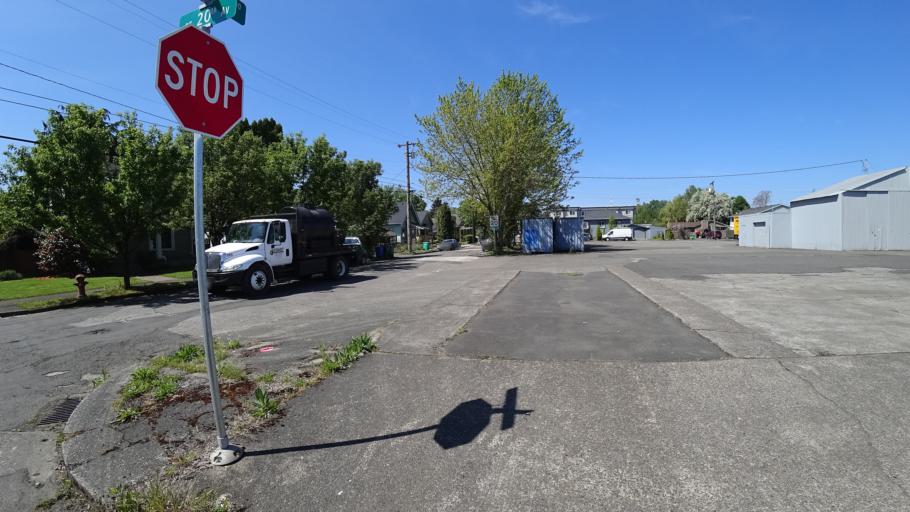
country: US
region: Oregon
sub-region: Clackamas County
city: Milwaukie
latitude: 45.4840
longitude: -122.6455
